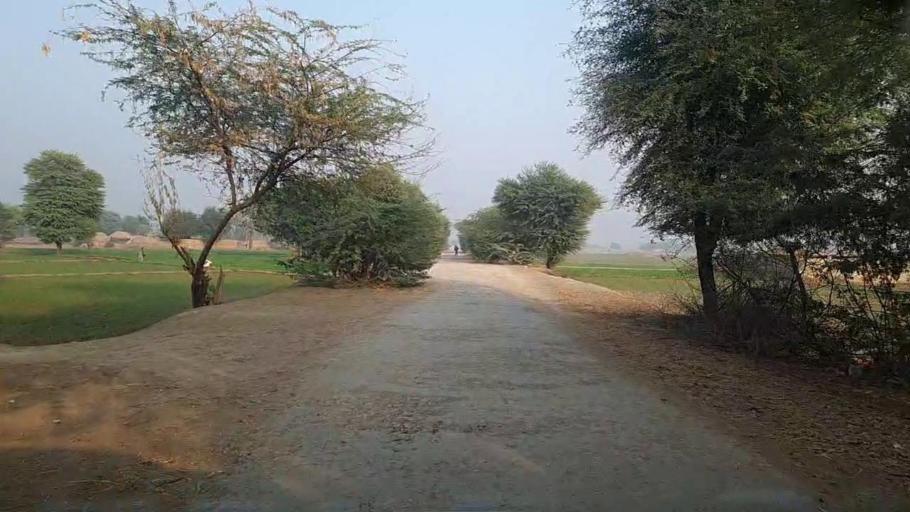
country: PK
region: Sindh
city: Bozdar
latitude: 27.0817
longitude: 68.5319
